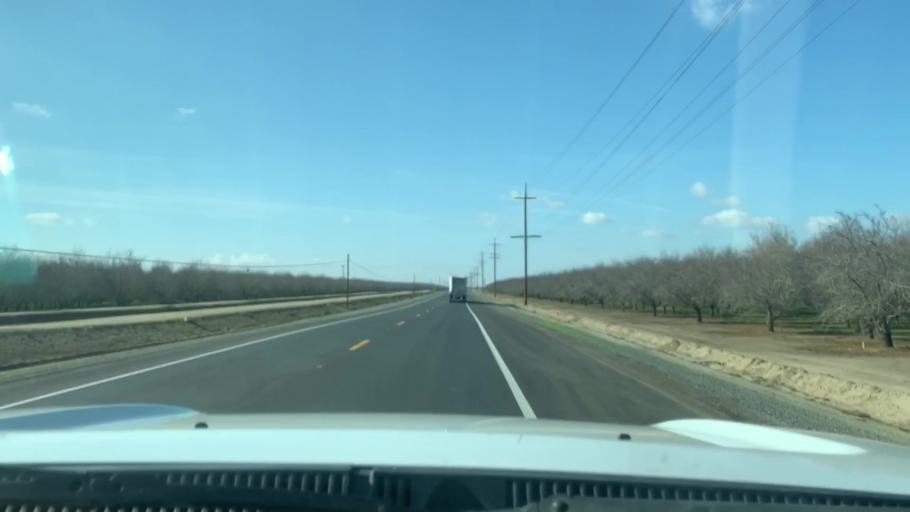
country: US
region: California
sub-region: Kern County
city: Wasco
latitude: 35.6018
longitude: -119.2826
